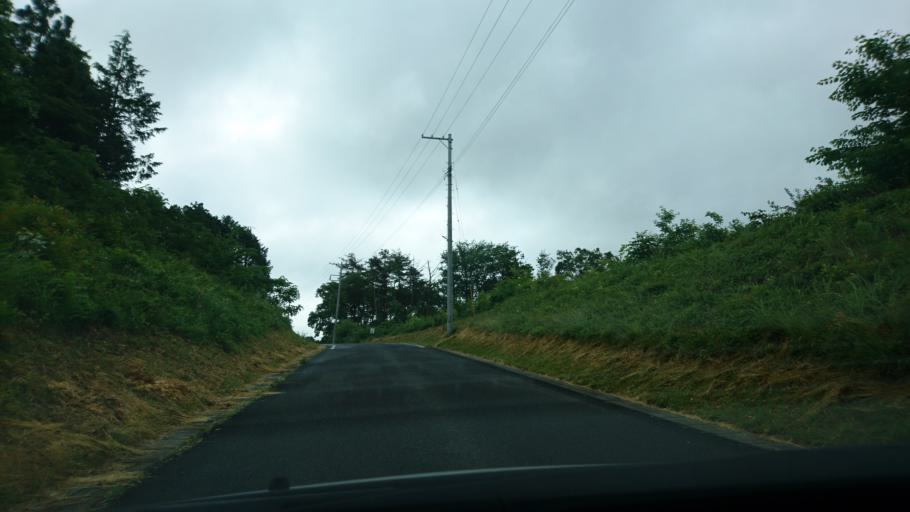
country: JP
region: Iwate
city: Ichinoseki
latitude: 38.9029
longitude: 141.1415
